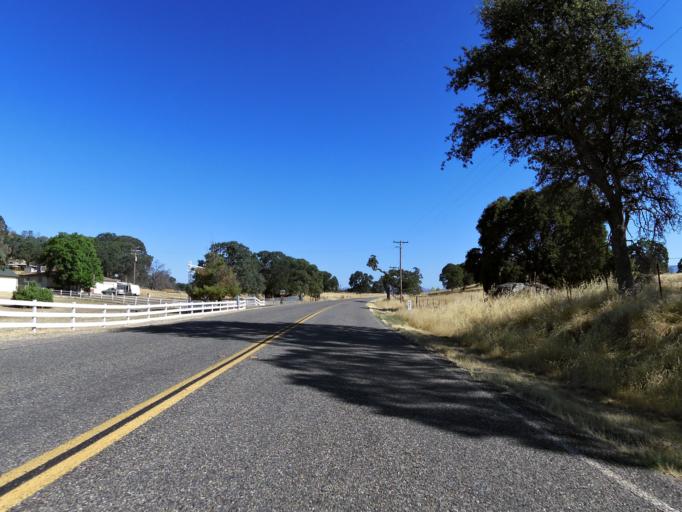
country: US
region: California
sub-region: Mariposa County
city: Mariposa
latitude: 37.4348
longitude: -120.1001
